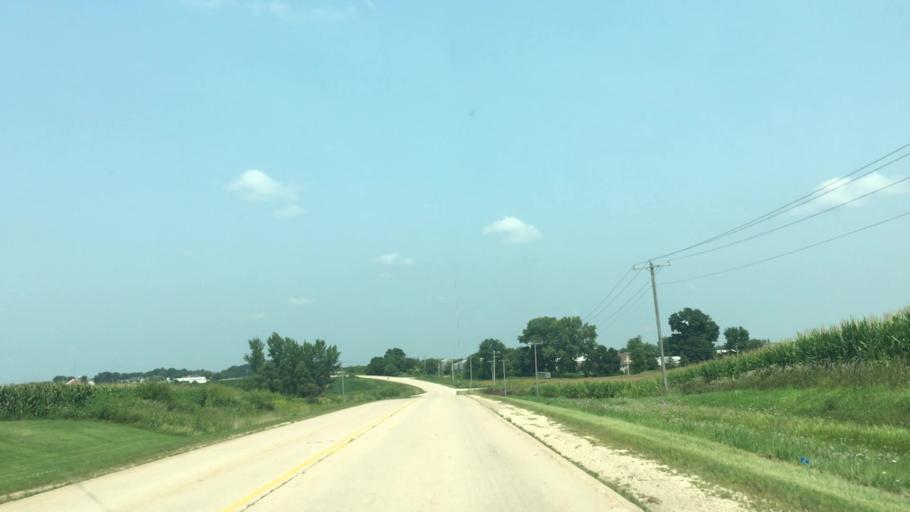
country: US
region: Iowa
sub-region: Fayette County
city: Oelwein
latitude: 42.6624
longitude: -91.8964
